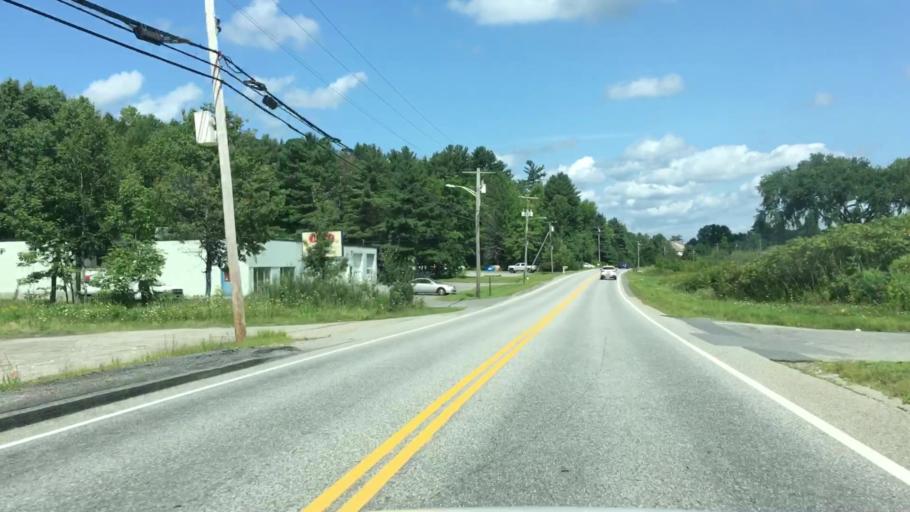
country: US
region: Maine
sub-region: Kennebec County
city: Augusta
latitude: 44.3225
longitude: -69.8167
